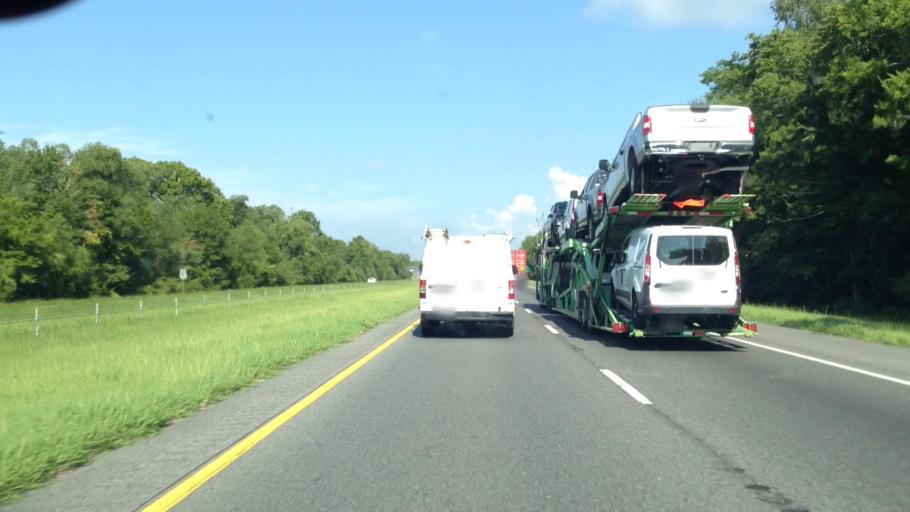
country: US
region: Louisiana
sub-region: Ascension Parish
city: Sorrento
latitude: 30.1518
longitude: -90.7946
